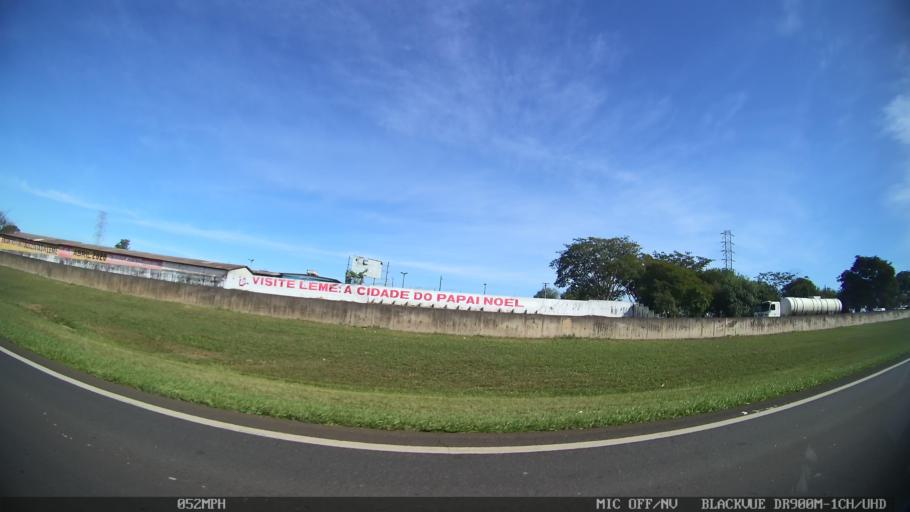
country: BR
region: Sao Paulo
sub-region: Leme
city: Leme
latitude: -22.1858
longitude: -47.3982
